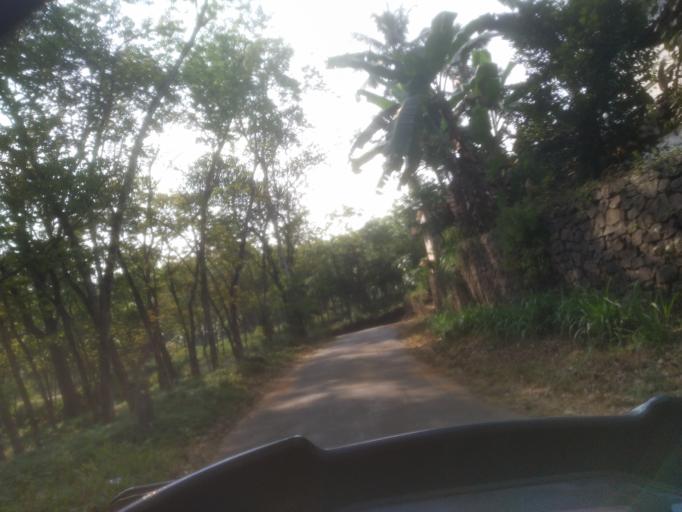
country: IN
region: Kerala
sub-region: Ernakulam
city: Piravam
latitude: 9.8435
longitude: 76.5269
